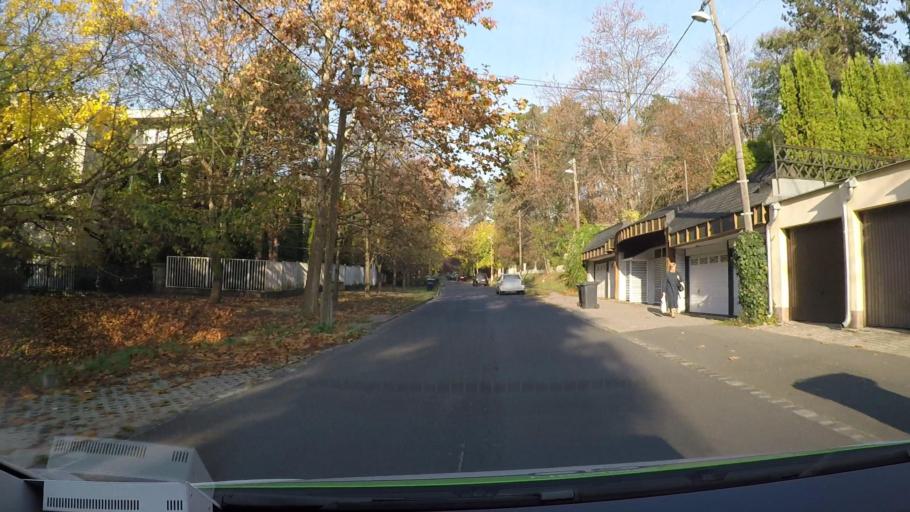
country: HU
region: Budapest
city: Budapest XII. keruelet
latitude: 47.5217
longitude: 18.9825
